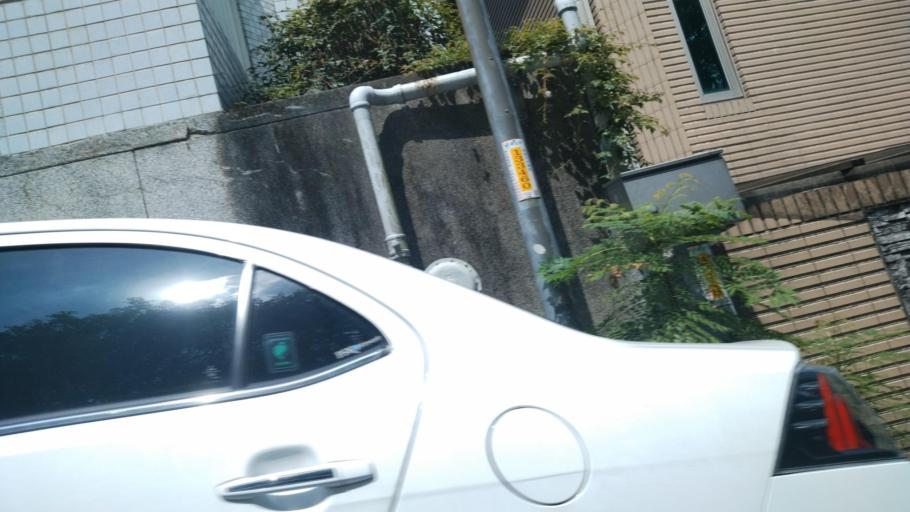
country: TW
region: Taipei
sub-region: Taipei
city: Banqiao
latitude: 24.9471
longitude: 121.5001
